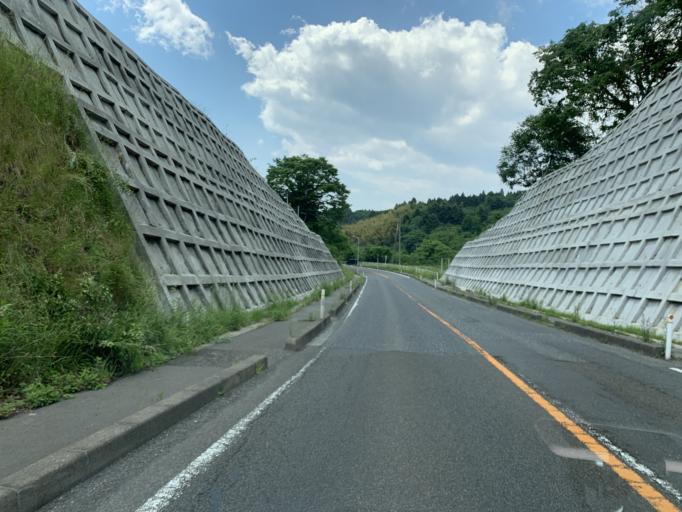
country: JP
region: Miyagi
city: Matsushima
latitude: 38.4051
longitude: 141.0670
